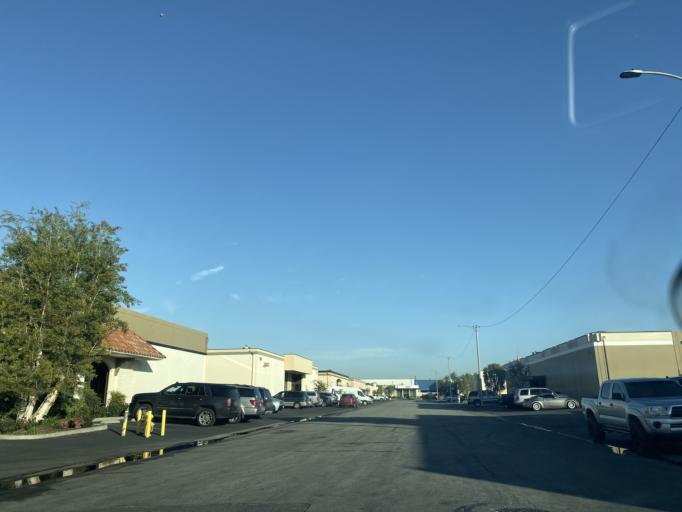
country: US
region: California
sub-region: Orange County
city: Fullerton
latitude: 33.8625
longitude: -117.9188
